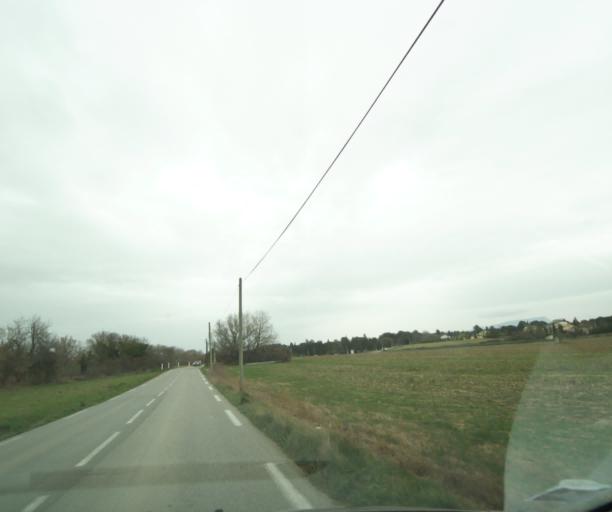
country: FR
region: Provence-Alpes-Cote d'Azur
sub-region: Departement des Bouches-du-Rhone
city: Eguilles
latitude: 43.5767
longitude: 5.4060
